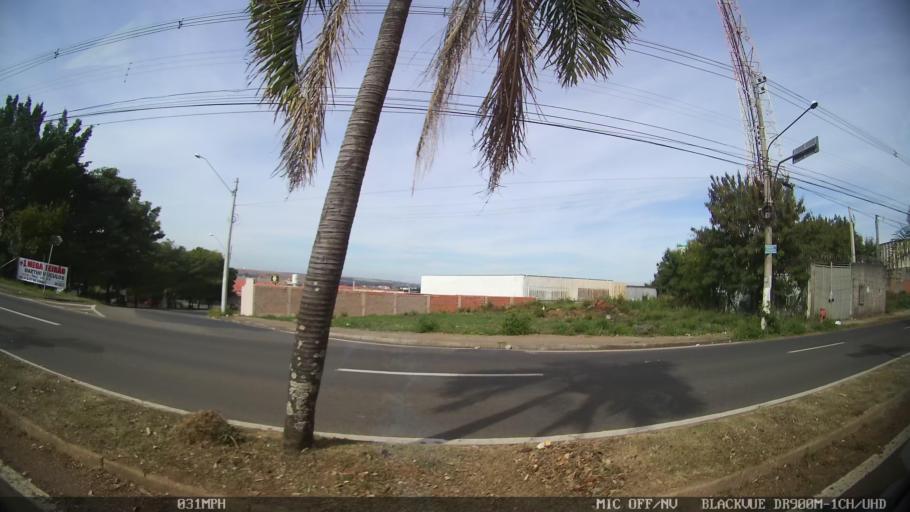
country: BR
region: Sao Paulo
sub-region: Piracicaba
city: Piracicaba
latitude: -22.7556
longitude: -47.6378
